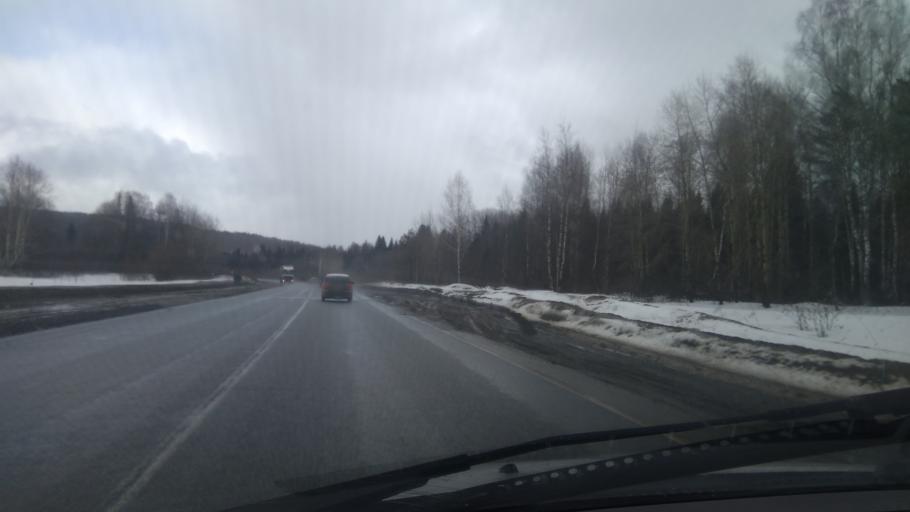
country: RU
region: Sverdlovsk
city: Ufimskiy
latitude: 56.7810
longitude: 58.4073
